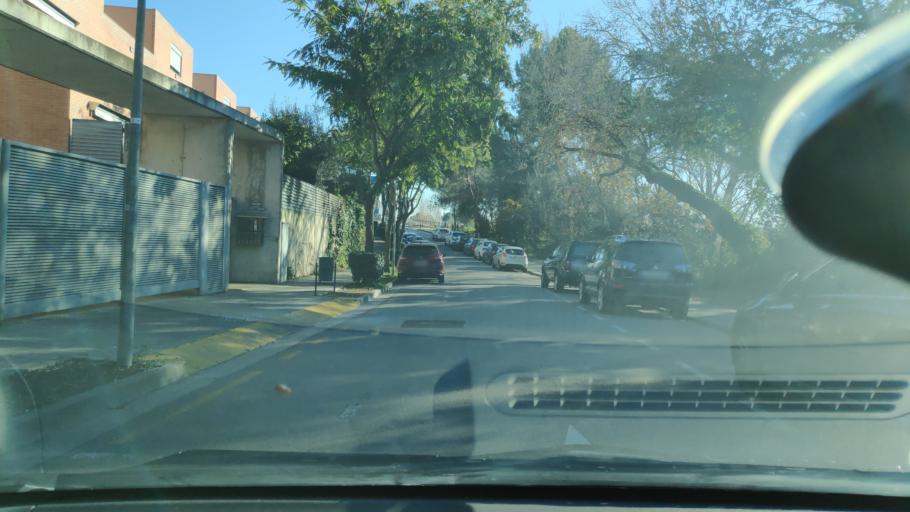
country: ES
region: Catalonia
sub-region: Provincia de Barcelona
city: Sant Quirze del Valles
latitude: 41.5407
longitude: 2.0686
